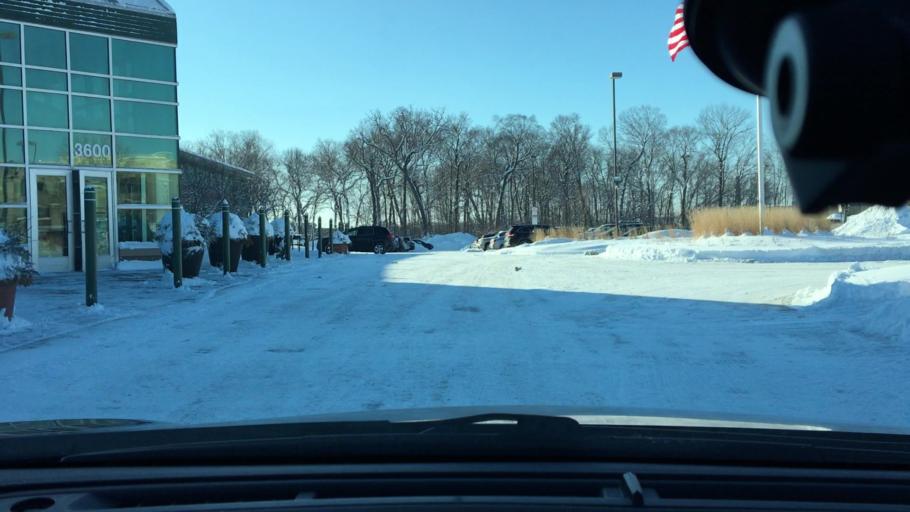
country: US
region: Minnesota
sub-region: Hennepin County
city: Plymouth
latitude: 45.0225
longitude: -93.4764
